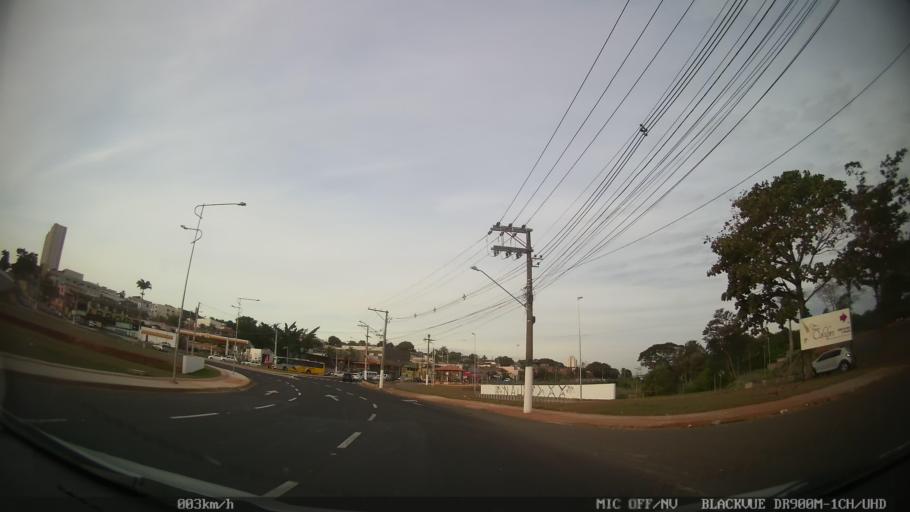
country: BR
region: Sao Paulo
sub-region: Limeira
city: Limeira
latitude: -22.5844
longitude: -47.4092
